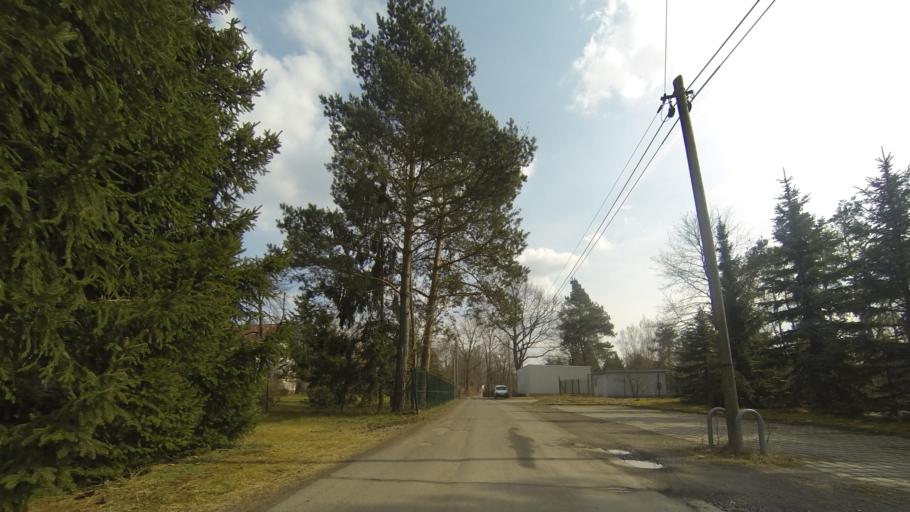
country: DE
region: Saxony
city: Radeburg
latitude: 51.2246
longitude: 13.7167
